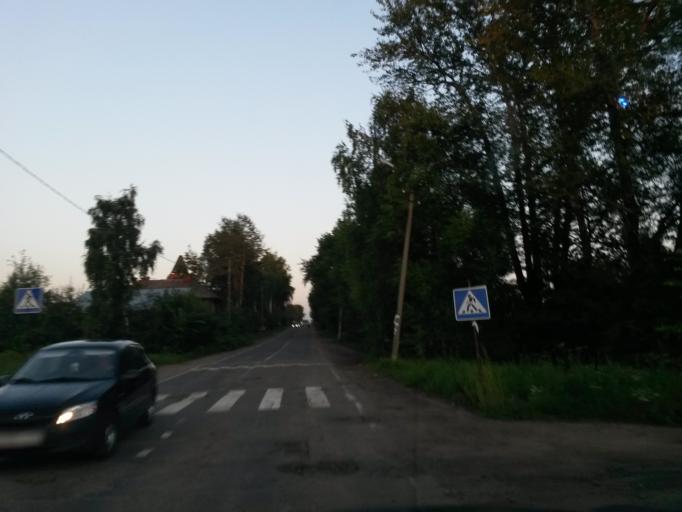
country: RU
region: Jaroslavl
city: Tutayev
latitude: 57.8872
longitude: 39.5400
